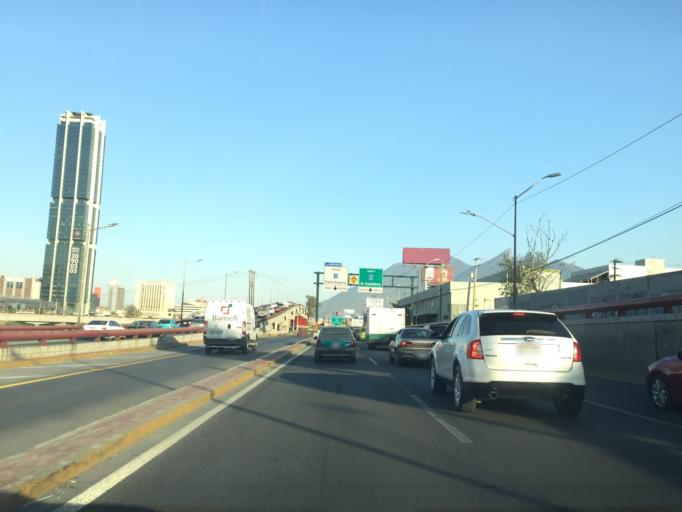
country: MX
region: Nuevo Leon
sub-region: Monterrey
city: Monterrey
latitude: 25.6640
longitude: -100.3237
